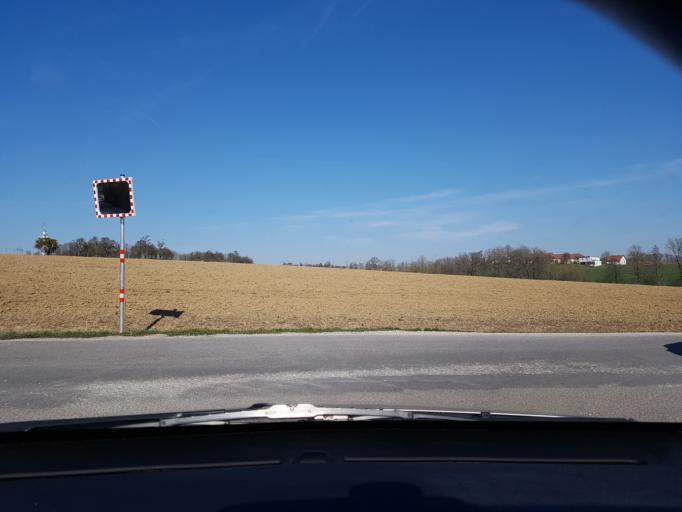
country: AT
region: Upper Austria
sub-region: Politischer Bezirk Linz-Land
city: Ansfelden
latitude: 48.1978
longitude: 14.3103
